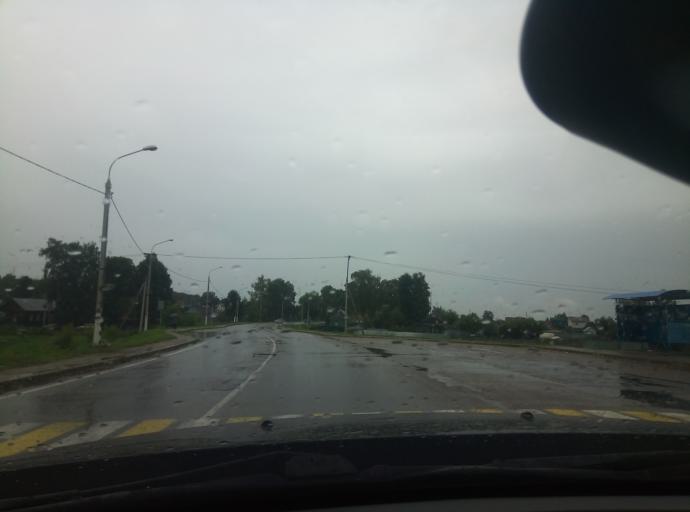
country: RU
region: Kaluga
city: Vysokinichi
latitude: 54.9089
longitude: 36.9223
